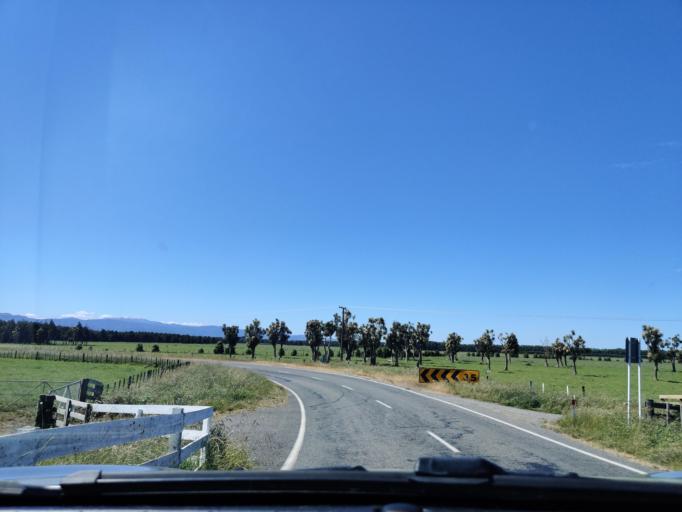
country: NZ
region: Wellington
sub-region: Upper Hutt City
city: Upper Hutt
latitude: -41.2861
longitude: 175.2691
